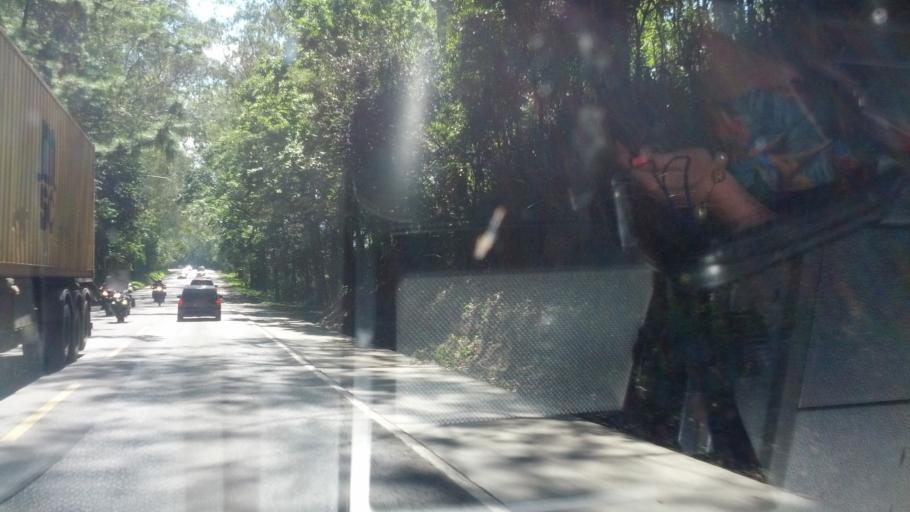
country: BR
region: Santa Catarina
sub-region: Rio Do Sul
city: Rio do Sul
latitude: -27.1694
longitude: -49.5665
